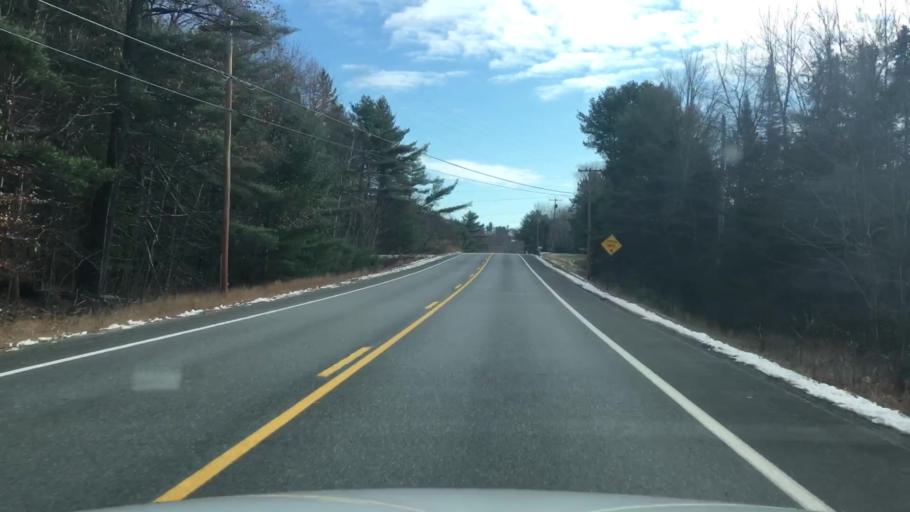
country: US
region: Maine
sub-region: Kennebec County
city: Wayne
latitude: 44.3415
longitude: -70.0263
